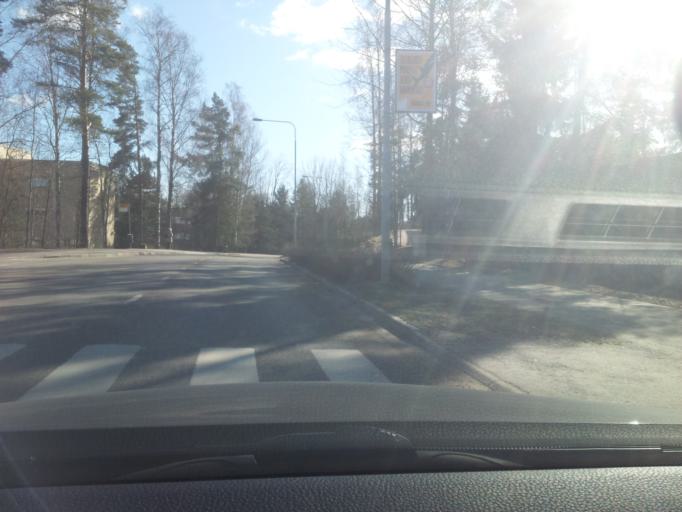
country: FI
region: Uusimaa
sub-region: Helsinki
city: Koukkuniemi
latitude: 60.1629
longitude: 24.7908
